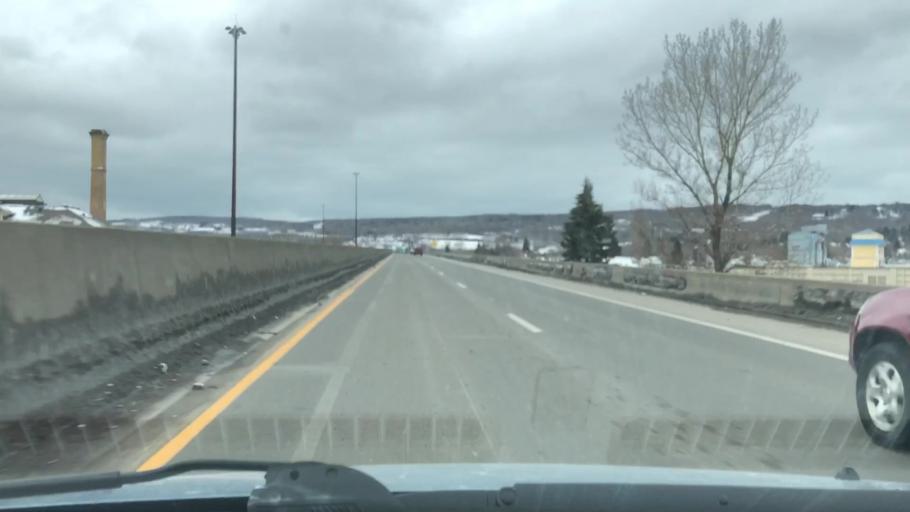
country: US
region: Minnesota
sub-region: Saint Louis County
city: Proctor
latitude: 46.7361
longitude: -92.1667
